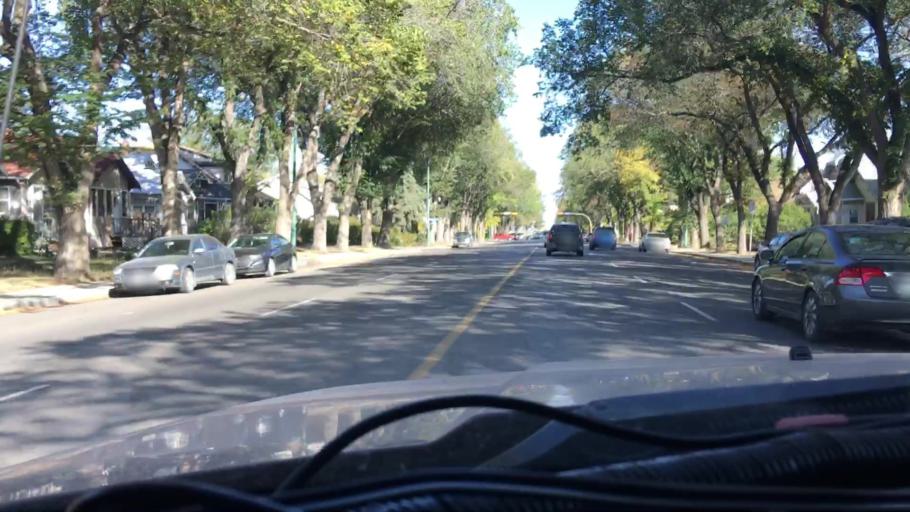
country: CA
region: Saskatchewan
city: Regina
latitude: 50.4551
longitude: -104.6337
